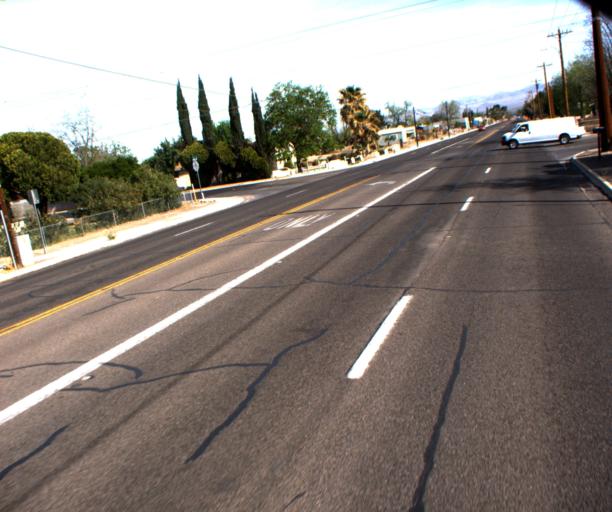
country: US
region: Arizona
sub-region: Graham County
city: Safford
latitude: 32.8163
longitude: -109.7076
